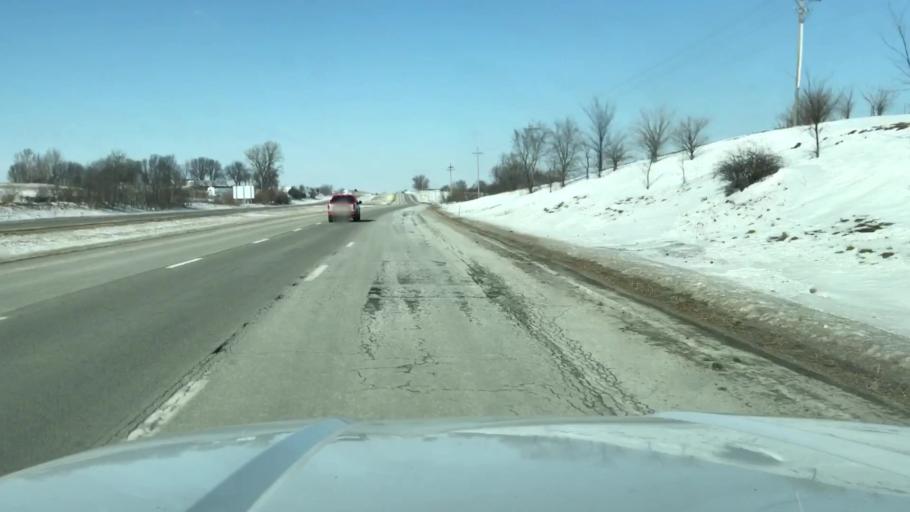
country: US
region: Missouri
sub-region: Andrew County
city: Savannah
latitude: 39.9646
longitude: -94.8640
